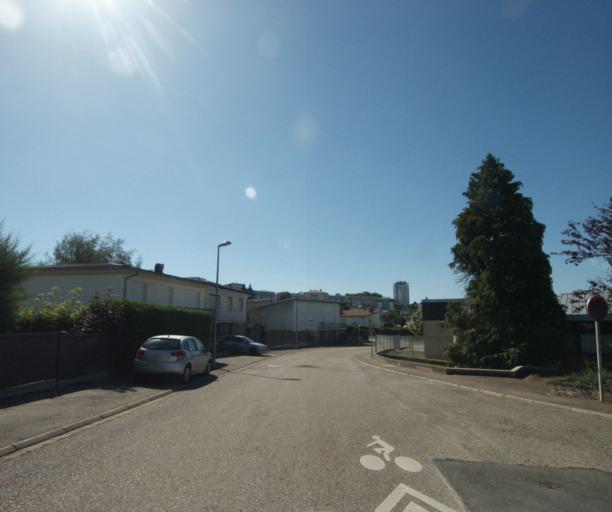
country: FR
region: Lorraine
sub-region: Departement des Vosges
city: Epinal
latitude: 48.1869
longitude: 6.4516
